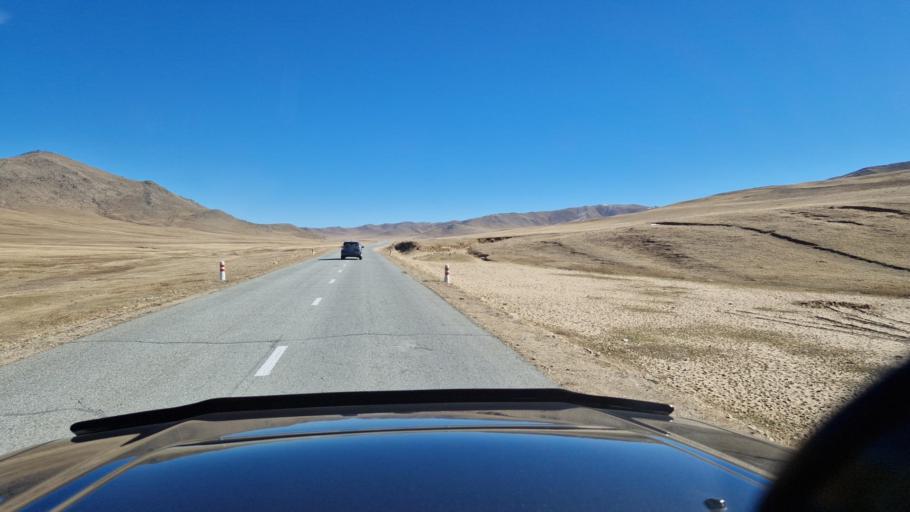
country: MN
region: Central Aimak
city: Bayandelger
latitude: 47.6936
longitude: 108.4914
